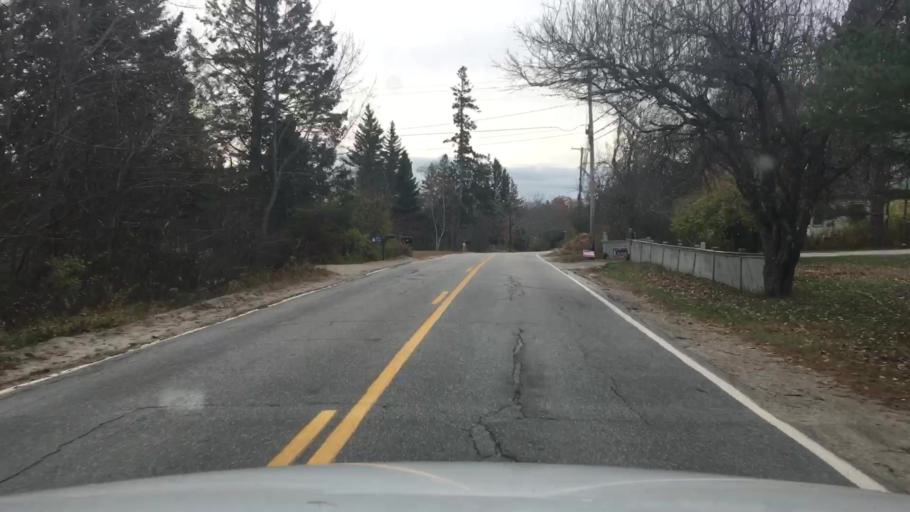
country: US
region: Maine
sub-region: Hancock County
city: Sedgwick
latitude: 44.3622
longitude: -68.5508
